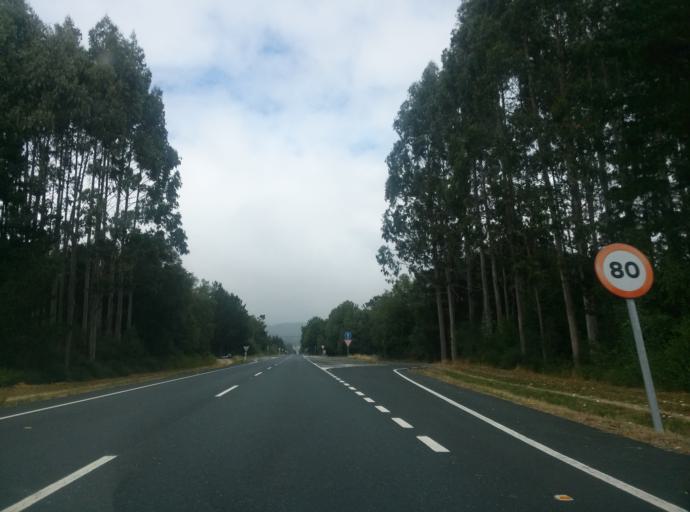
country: ES
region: Galicia
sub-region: Provincia de Lugo
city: Muras
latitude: 43.4105
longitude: -7.7742
